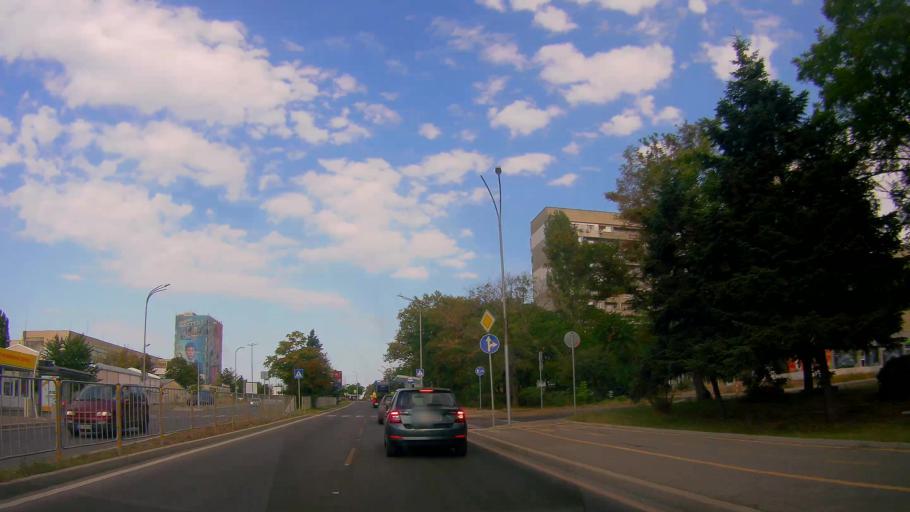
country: BG
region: Burgas
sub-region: Obshtina Burgas
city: Burgas
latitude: 42.5191
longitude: 27.4430
